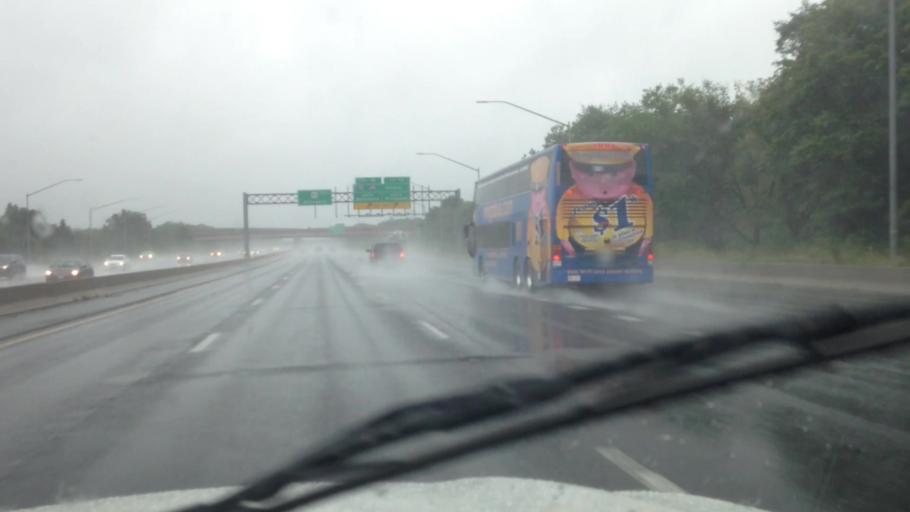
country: US
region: Maryland
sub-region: Prince George's County
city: Glenarden
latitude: 38.9448
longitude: -76.8654
